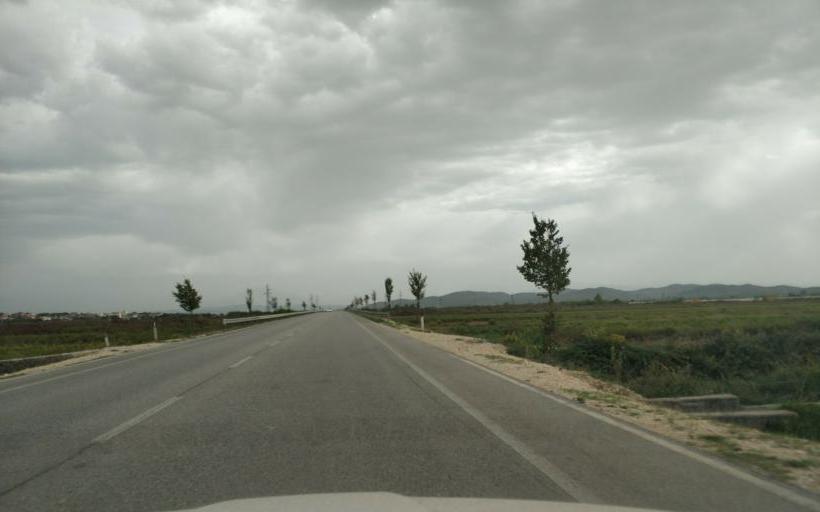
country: AL
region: Fier
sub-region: Rrethi i Fierit
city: Frakulla e Madhe
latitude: 40.6458
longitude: 19.4981
